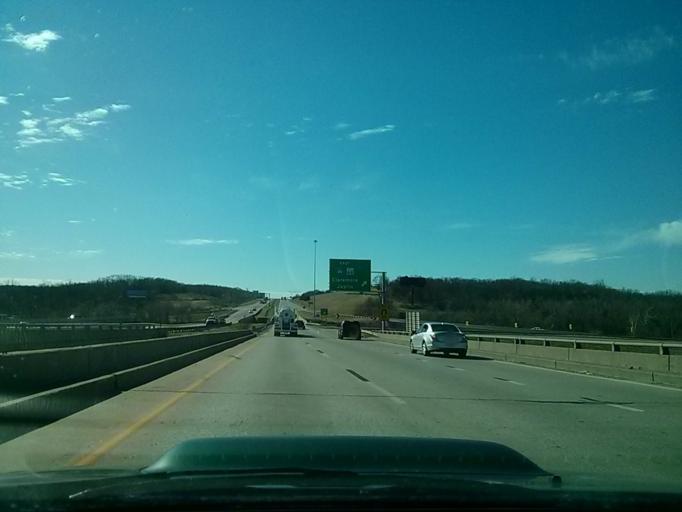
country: US
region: Oklahoma
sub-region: Tulsa County
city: Oakhurst
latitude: 36.0892
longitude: -96.0066
